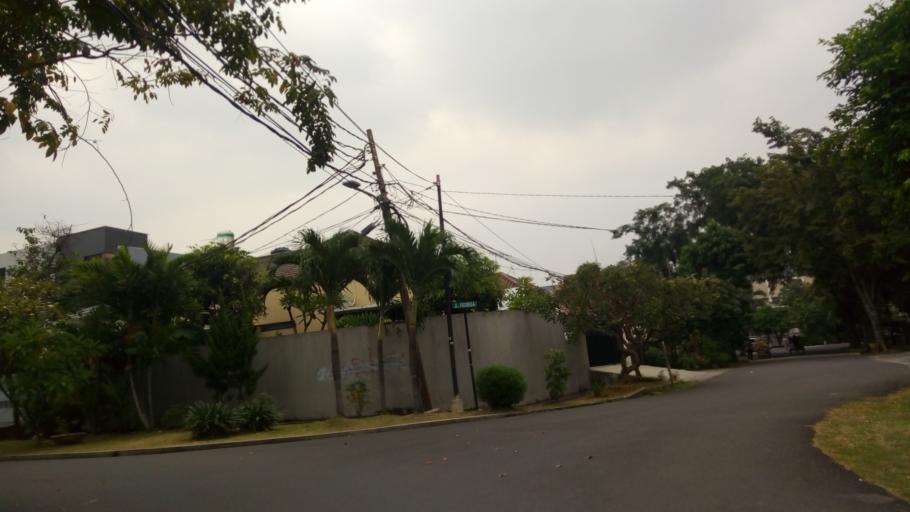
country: ID
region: Jakarta Raya
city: Jakarta
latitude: -6.1531
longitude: 106.8407
